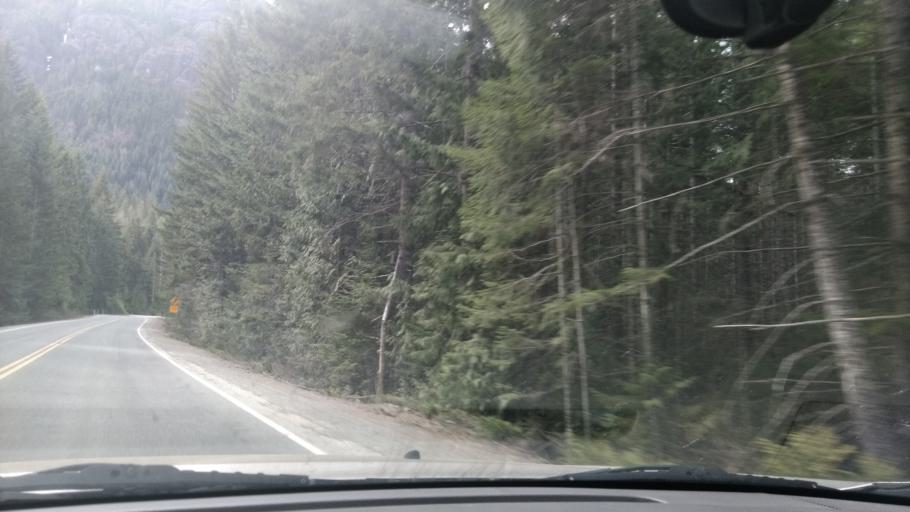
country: CA
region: British Columbia
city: Campbell River
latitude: 49.8447
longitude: -125.6407
